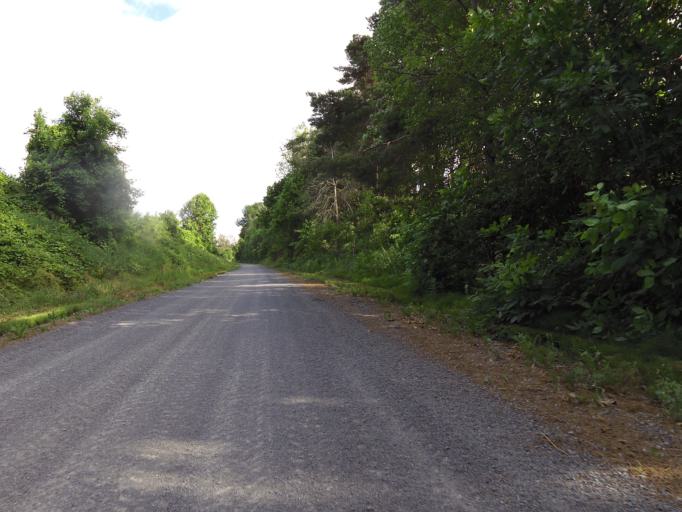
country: CA
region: Ontario
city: Arnprior
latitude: 45.3156
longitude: -76.2843
